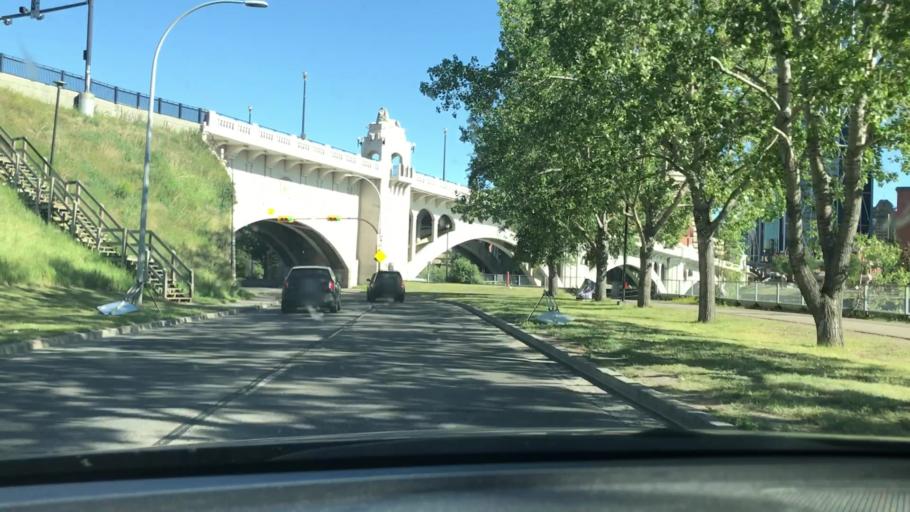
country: CA
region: Alberta
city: Calgary
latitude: 51.0544
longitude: -114.0633
